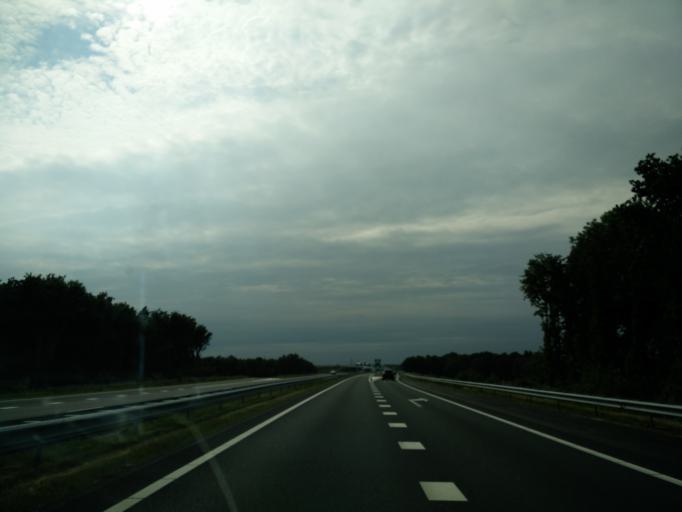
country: NL
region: Drenthe
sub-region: Gemeente Assen
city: Assen
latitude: 52.9694
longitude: 6.5600
